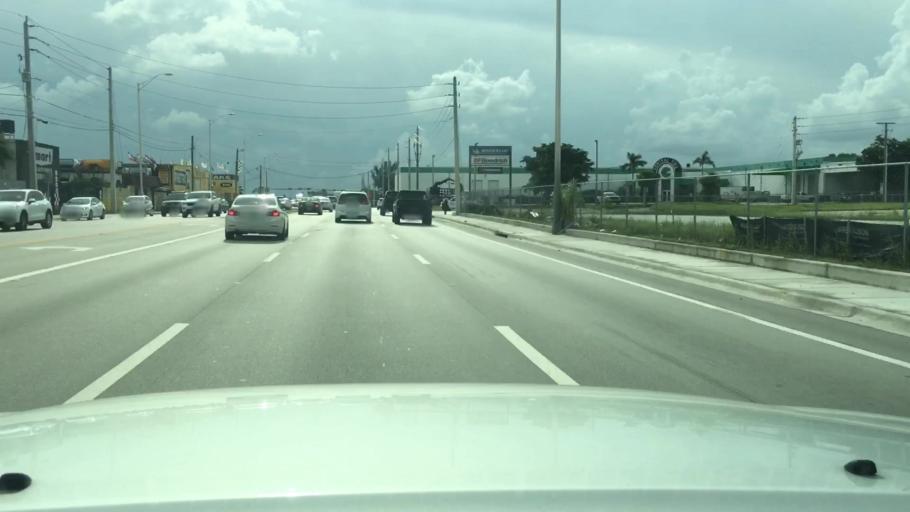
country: US
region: Florida
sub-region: Miami-Dade County
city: Hialeah Gardens
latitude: 25.8409
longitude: -80.3306
